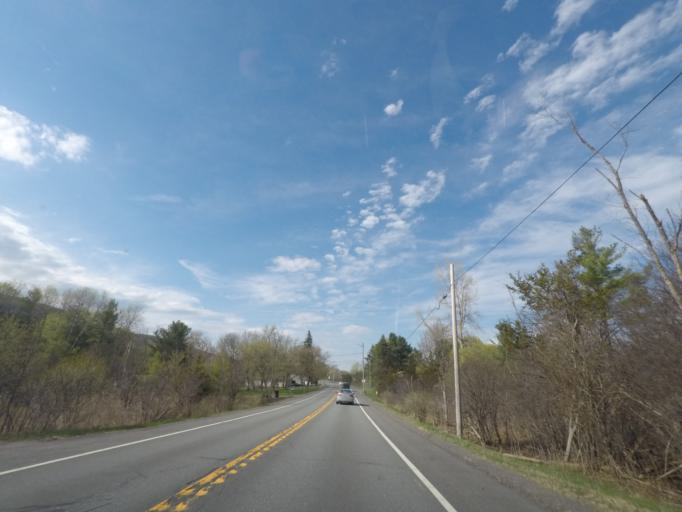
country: US
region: New York
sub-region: Albany County
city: Voorheesville
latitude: 42.6086
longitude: -73.9712
